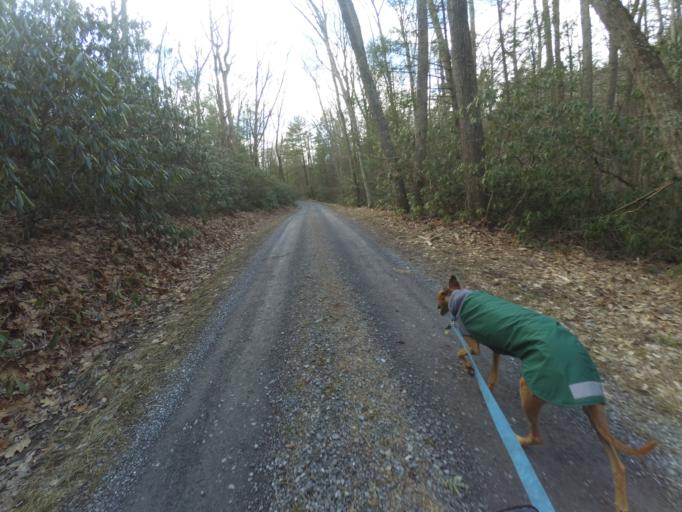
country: US
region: Pennsylvania
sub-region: Centre County
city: Boalsburg
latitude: 40.7508
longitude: -77.7076
